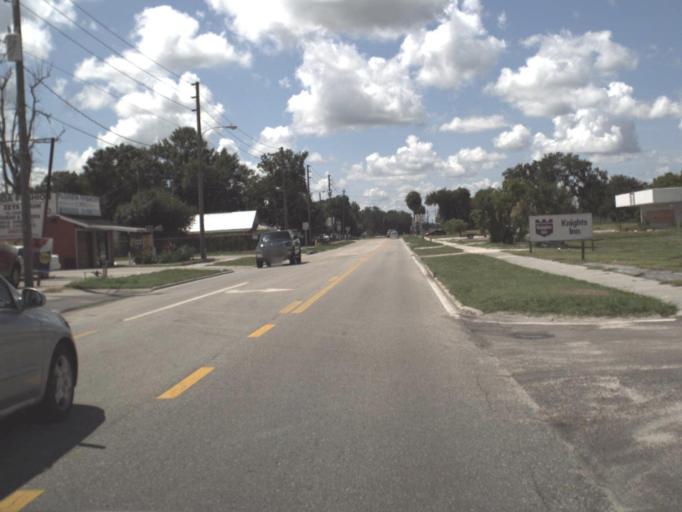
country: US
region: Florida
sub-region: DeSoto County
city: Arcadia
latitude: 27.2072
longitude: -81.8619
